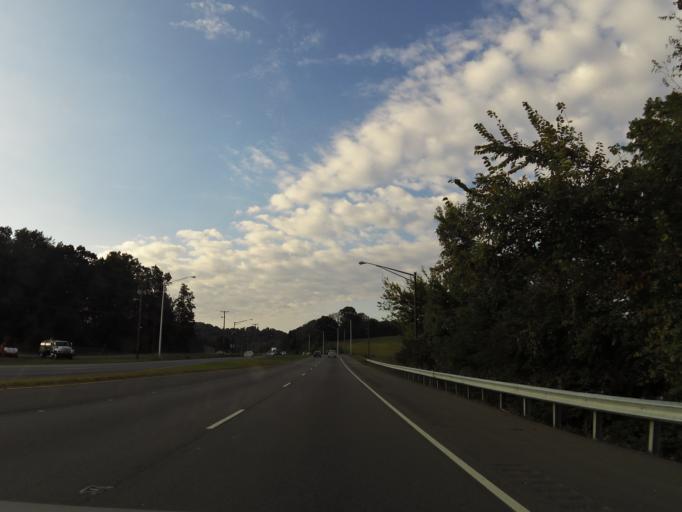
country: US
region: Tennessee
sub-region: Knox County
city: Knoxville
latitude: 35.9004
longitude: -83.9539
